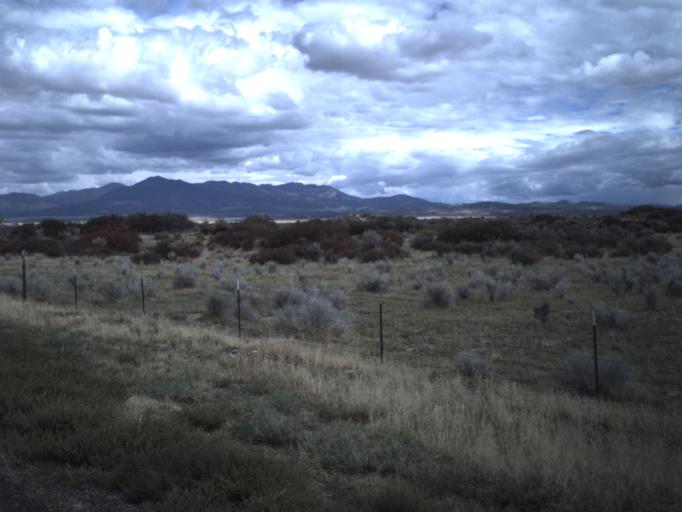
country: US
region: Utah
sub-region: Millard County
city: Fillmore
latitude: 39.1295
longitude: -112.4092
